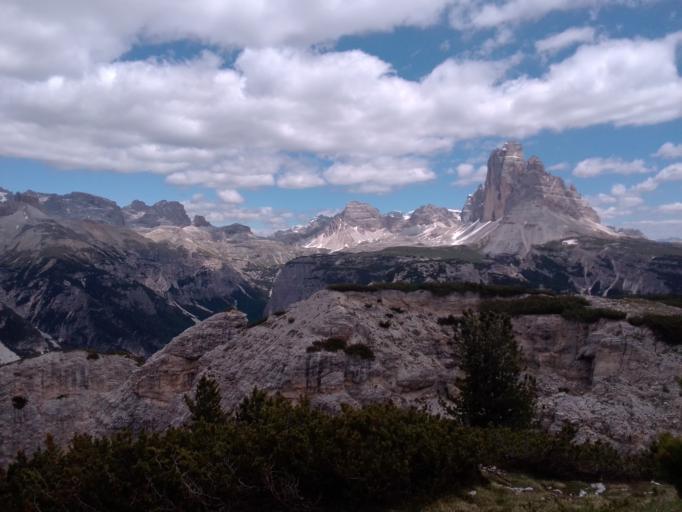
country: IT
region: Trentino-Alto Adige
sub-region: Bolzano
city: Dobbiaco
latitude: 46.6228
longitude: 12.2484
